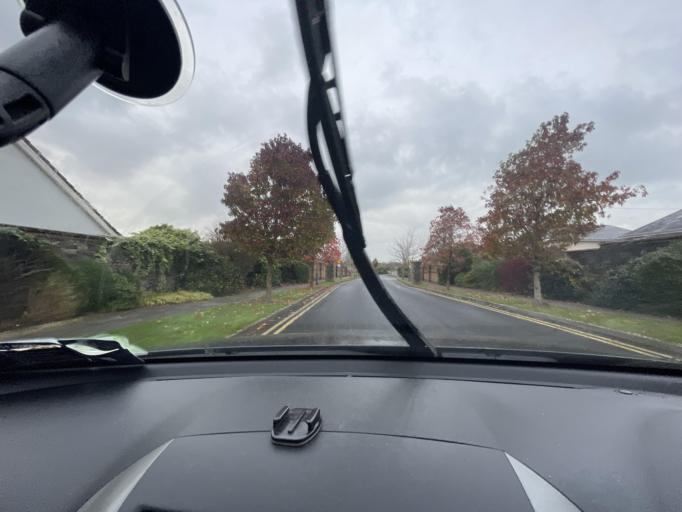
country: IE
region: Ulster
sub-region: An Cabhan
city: Virginia
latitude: 53.8363
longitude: -7.0755
